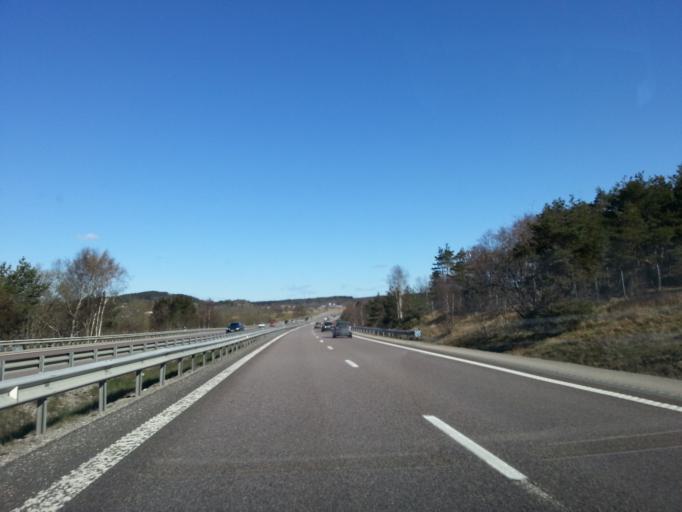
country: SE
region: Vaestra Goetaland
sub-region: Stenungsunds Kommun
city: Stora Hoga
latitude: 58.0078
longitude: 11.8438
